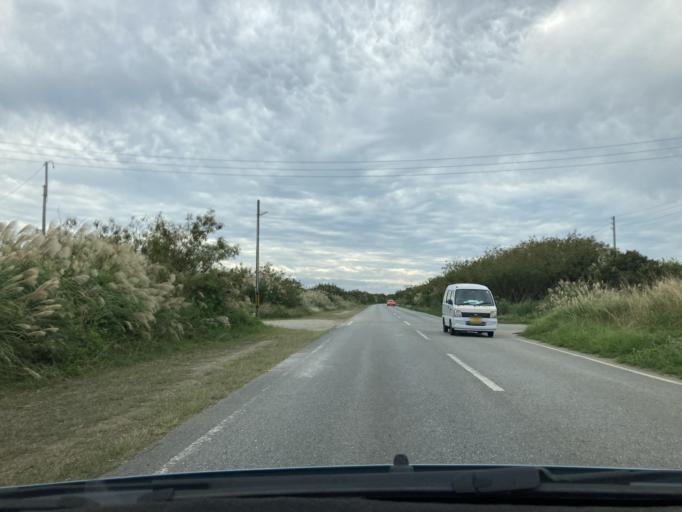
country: JP
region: Okinawa
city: Okinawa
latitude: 26.3918
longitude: 127.7411
